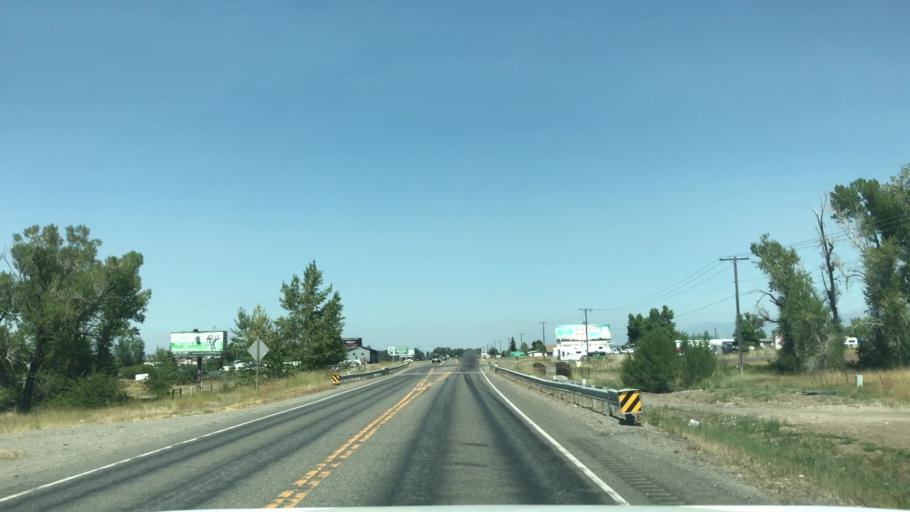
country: US
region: Montana
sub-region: Gallatin County
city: Four Corners
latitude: 45.5970
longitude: -111.1966
